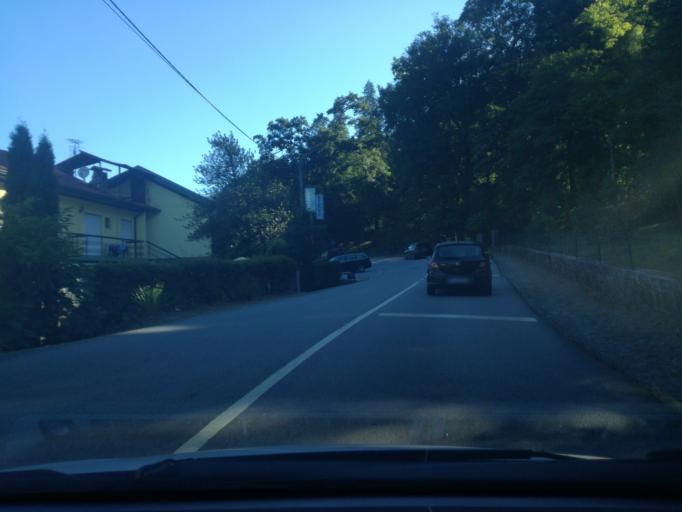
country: PT
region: Braga
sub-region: Vieira do Minho
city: Real
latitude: 41.7147
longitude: -8.1673
